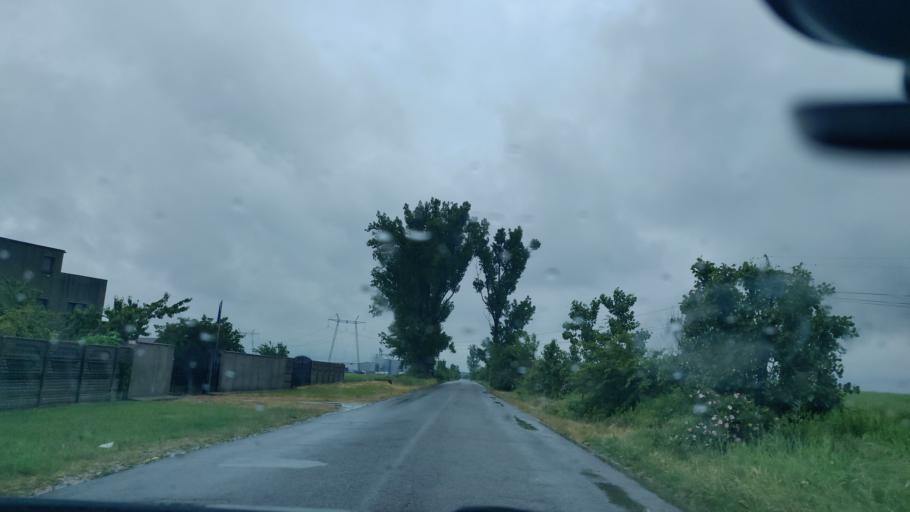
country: RO
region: Giurgiu
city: Iepuresti
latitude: 44.2696
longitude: 25.8447
